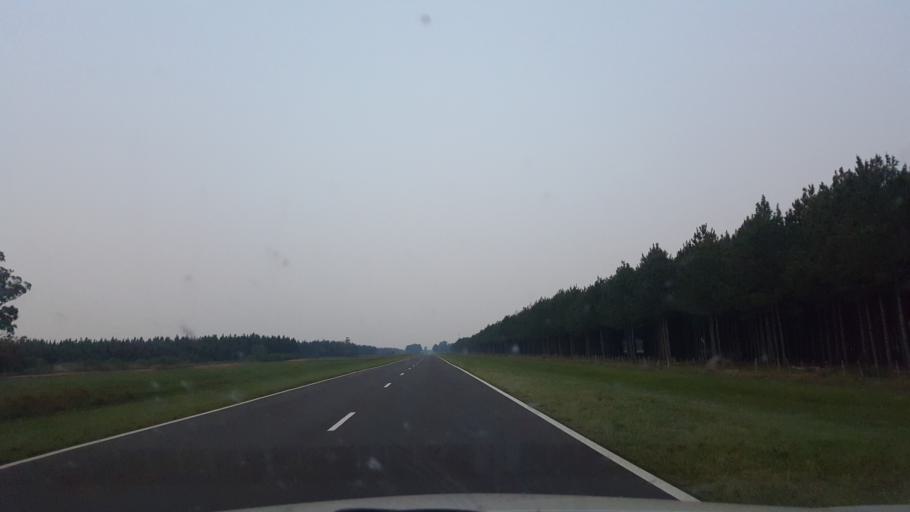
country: PY
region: Misiones
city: Ayolas
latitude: -27.6227
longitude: -56.9437
